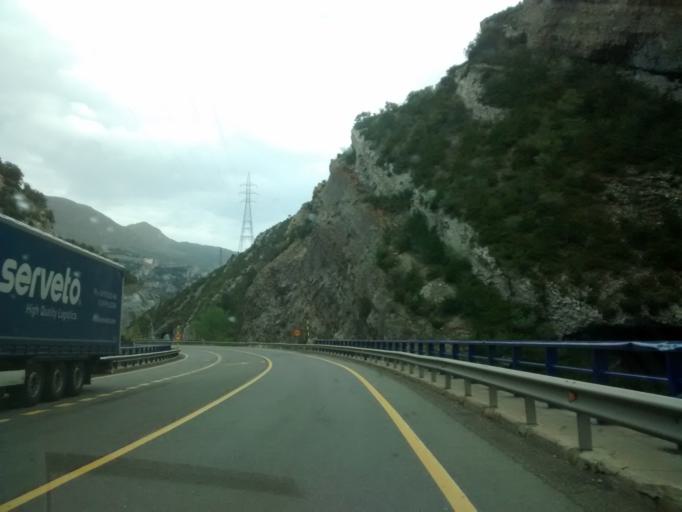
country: ES
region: Aragon
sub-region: Provincia de Huesca
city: Arguis
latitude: 42.3019
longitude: -0.4293
